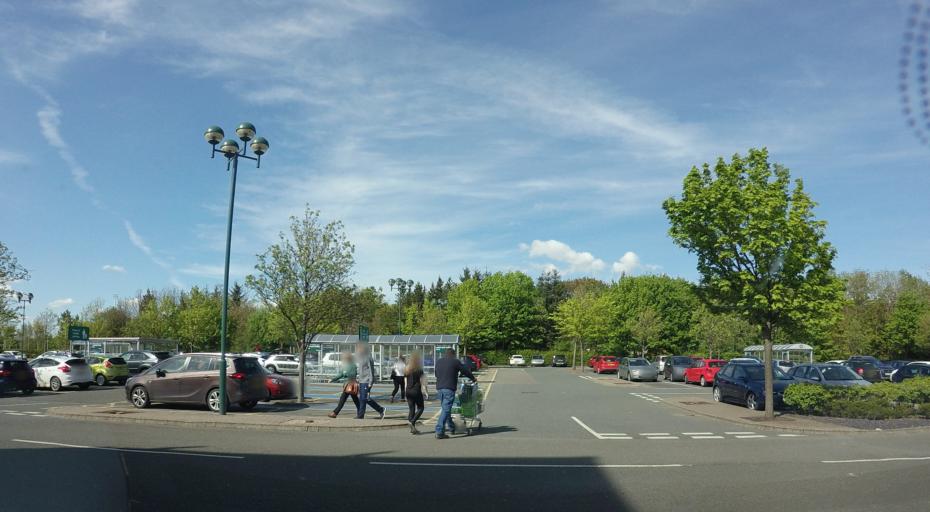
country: GB
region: Scotland
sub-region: Stirling
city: Bannockburn
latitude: 56.1162
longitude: -3.9093
